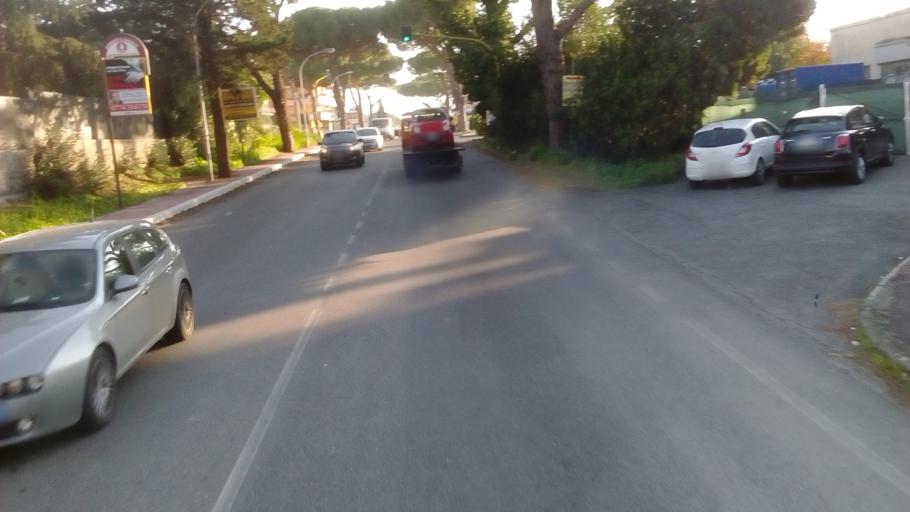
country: IT
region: Latium
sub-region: Citta metropolitana di Roma Capitale
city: Marino
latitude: 41.7618
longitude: 12.6161
